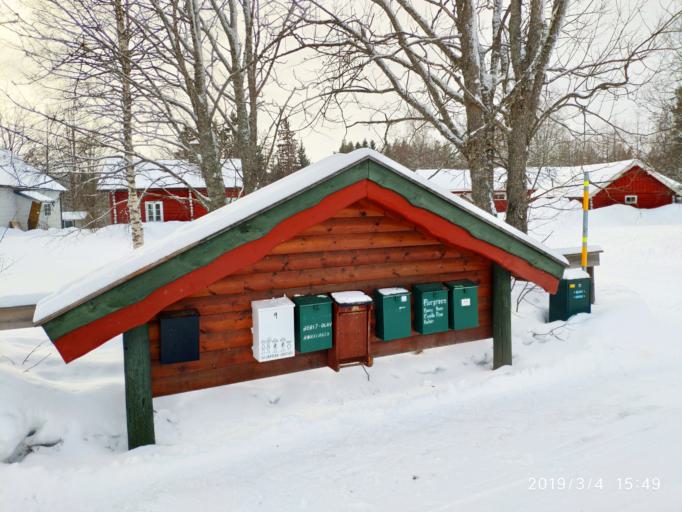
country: NO
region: Hedmark
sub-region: Trysil
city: Innbygda
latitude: 61.2560
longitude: 12.5298
